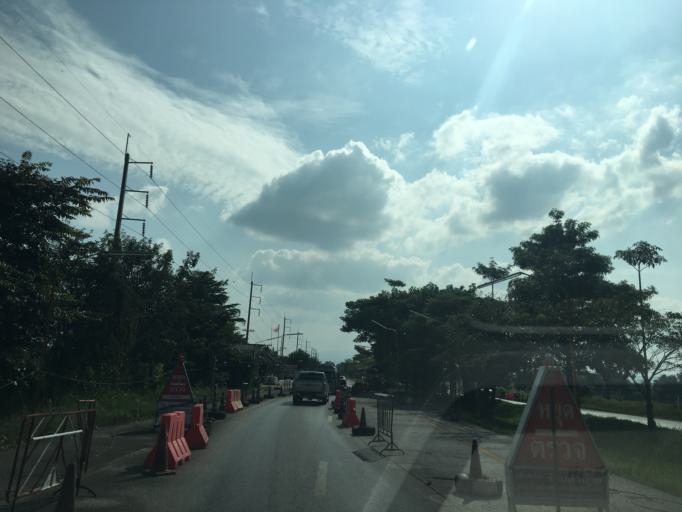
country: TH
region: Chiang Rai
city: Mae Lao
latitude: 19.7324
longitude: 99.7193
